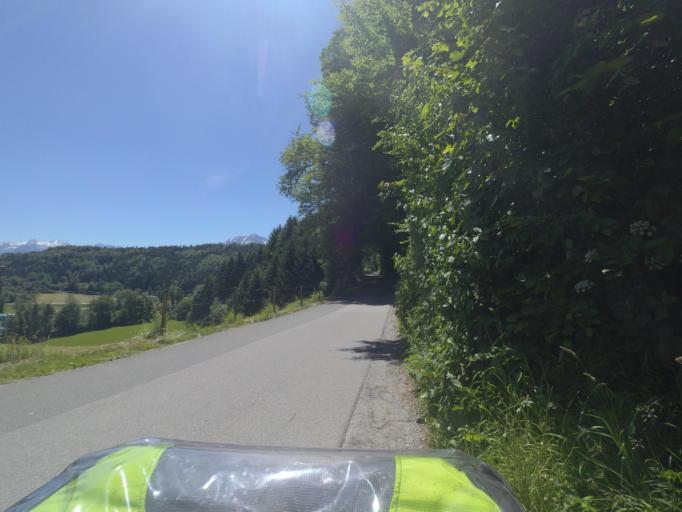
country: AT
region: Salzburg
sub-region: Politischer Bezirk Hallein
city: Oberalm
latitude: 47.7036
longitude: 13.1159
